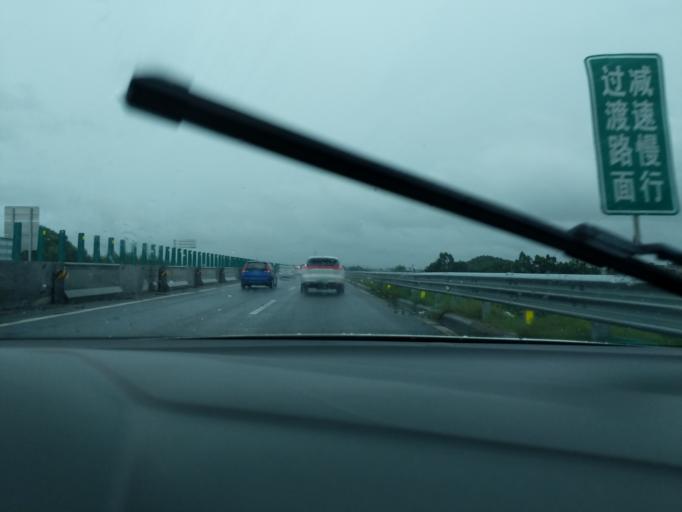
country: CN
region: Guangdong
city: Yueshan
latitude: 22.4613
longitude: 112.6893
